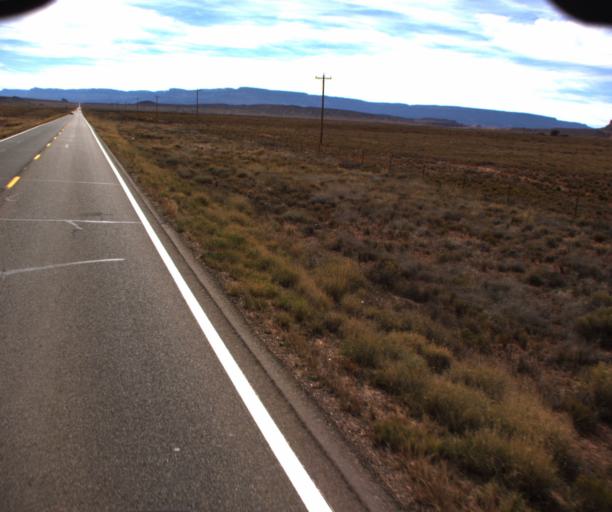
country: US
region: Arizona
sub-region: Navajo County
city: Kayenta
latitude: 36.8092
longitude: -110.2333
